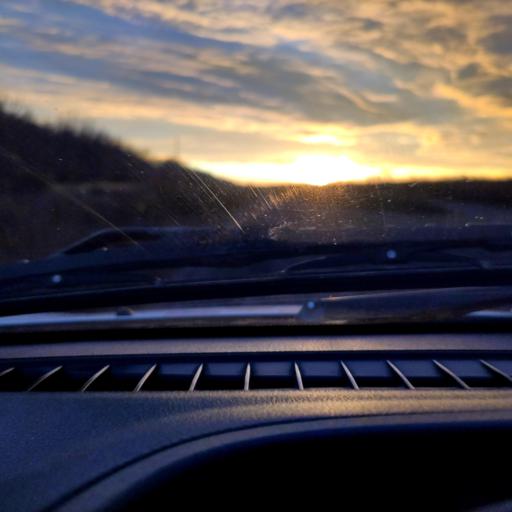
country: RU
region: Samara
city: Tol'yatti
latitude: 53.5972
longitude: 49.4655
